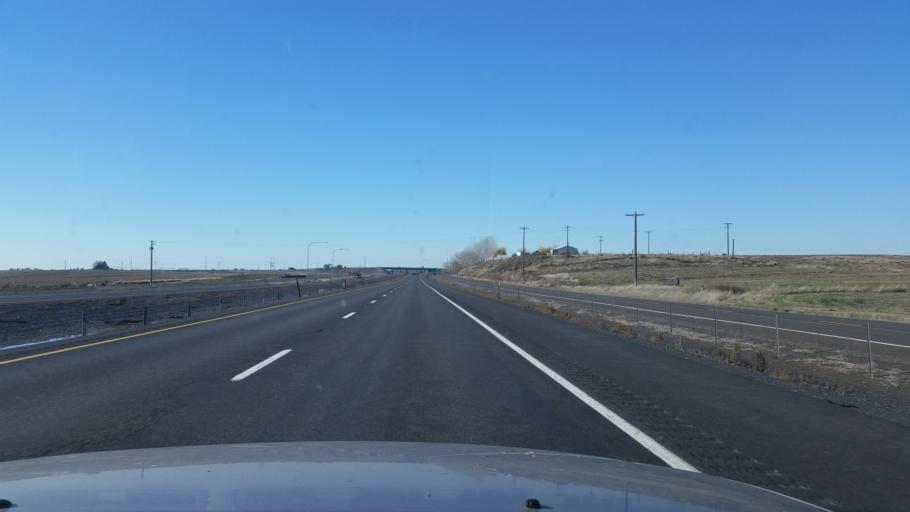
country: US
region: Washington
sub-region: Grant County
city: Warden
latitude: 47.0856
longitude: -119.0329
